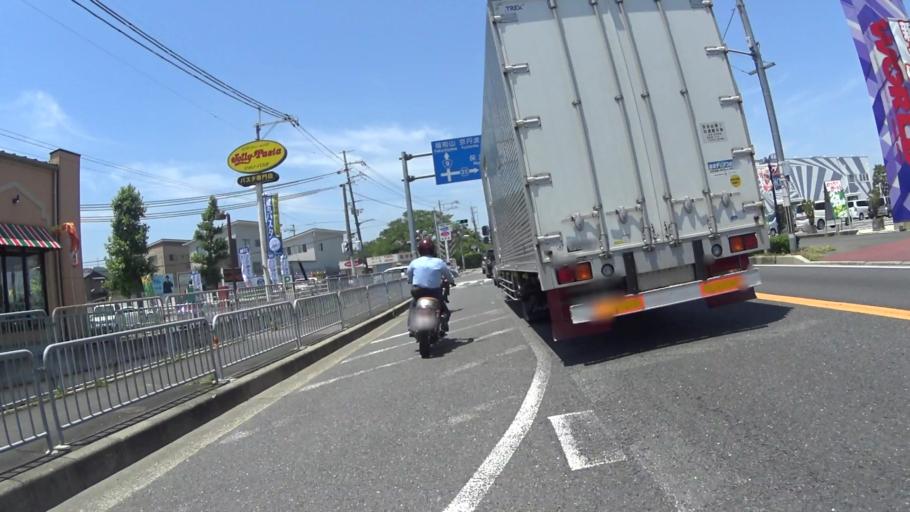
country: JP
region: Kyoto
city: Kameoka
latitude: 35.0054
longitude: 135.5843
